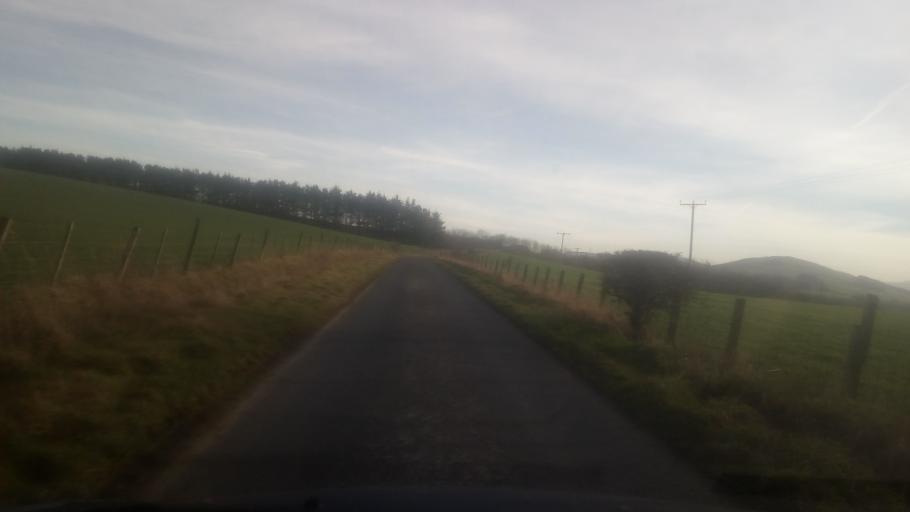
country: GB
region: Scotland
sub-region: The Scottish Borders
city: Jedburgh
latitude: 55.4331
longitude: -2.6265
